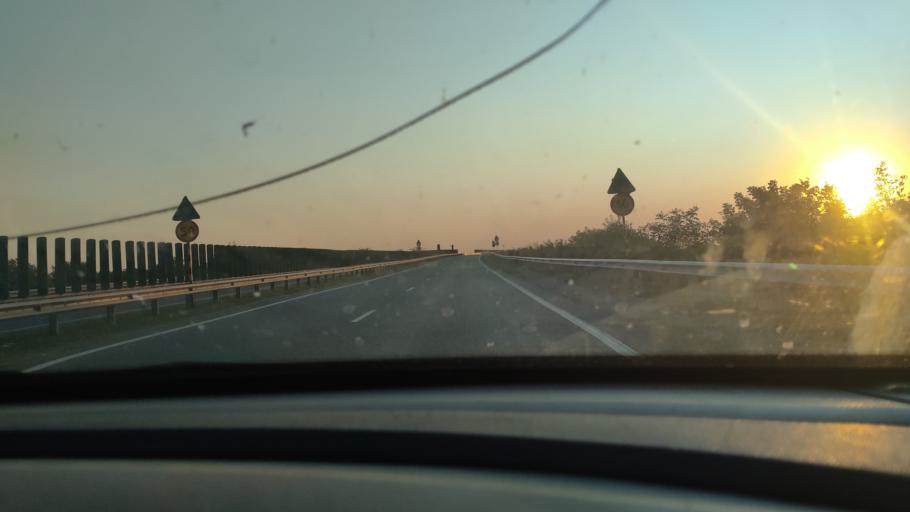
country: RU
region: Krasnodarskiy
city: Timashevsk
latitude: 45.6029
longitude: 38.9763
